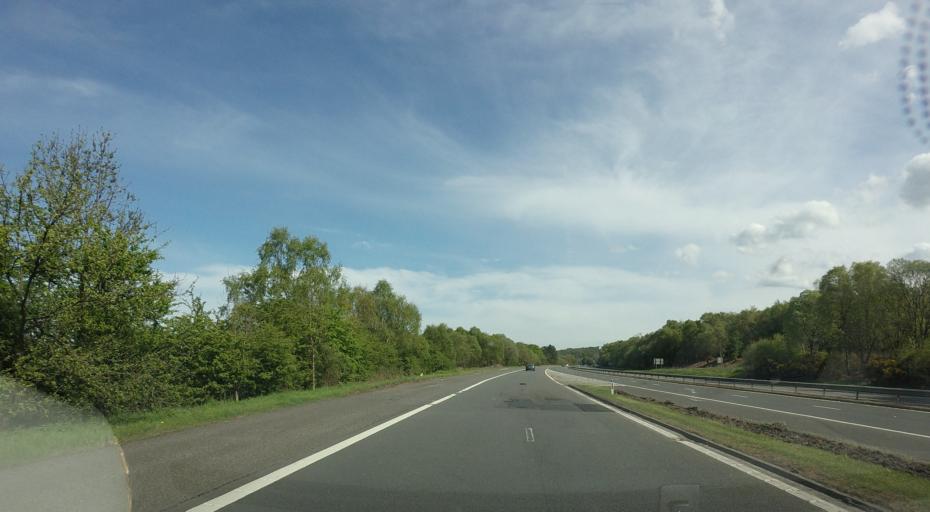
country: GB
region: Scotland
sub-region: Stirling
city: Bannockburn
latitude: 56.0764
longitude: -3.9141
